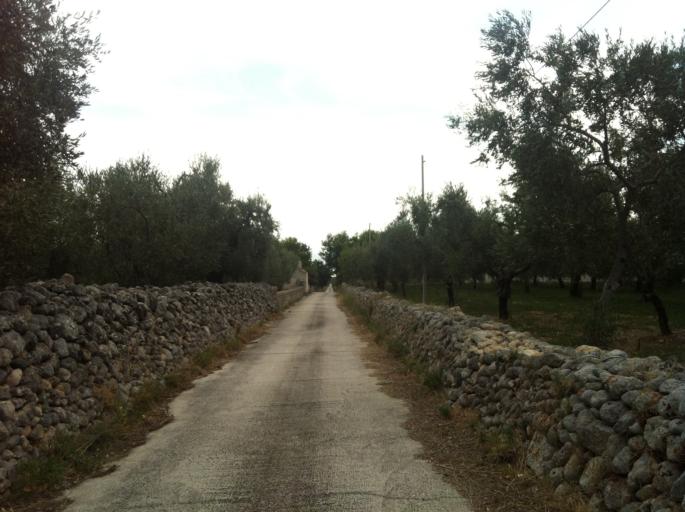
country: IT
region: Apulia
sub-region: Provincia di Foggia
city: Monte Sant'Angelo
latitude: 41.6611
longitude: 15.9536
